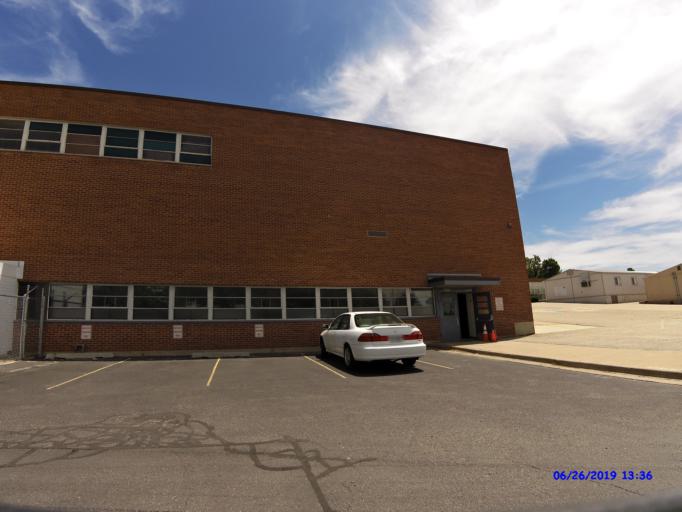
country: US
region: Utah
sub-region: Weber County
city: South Ogden
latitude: 41.2041
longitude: -111.9596
